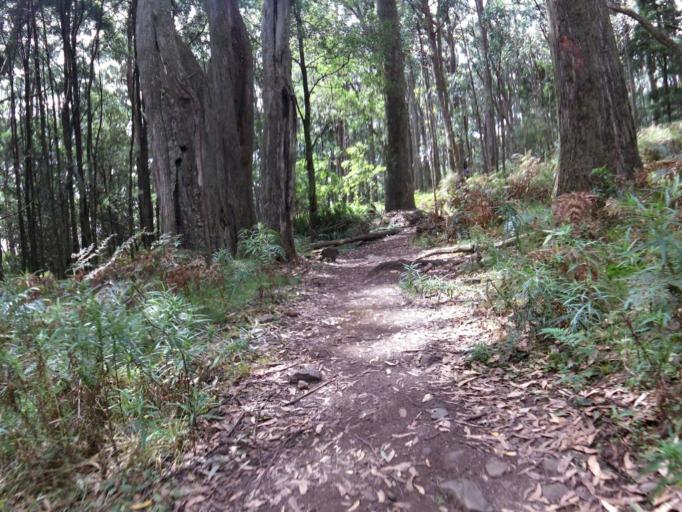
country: AU
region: Victoria
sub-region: Hume
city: Sunbury
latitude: -37.3715
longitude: 144.5817
